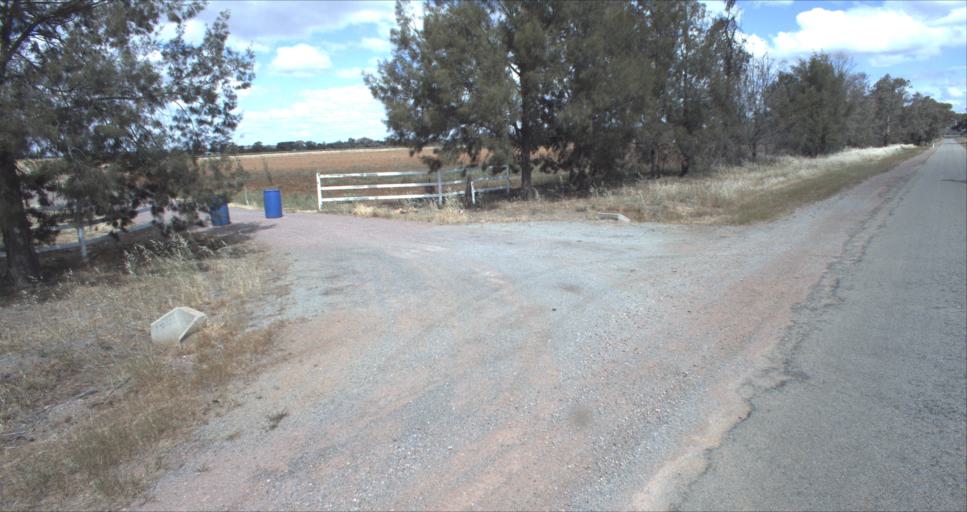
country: AU
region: New South Wales
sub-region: Leeton
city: Leeton
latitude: -34.5850
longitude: 146.3962
